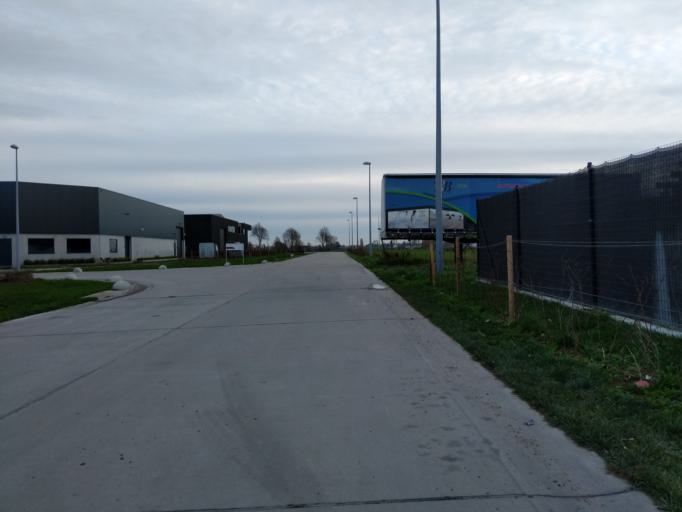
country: BE
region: Flanders
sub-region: Provincie West-Vlaanderen
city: Ruiselede
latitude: 51.0385
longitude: 3.4033
